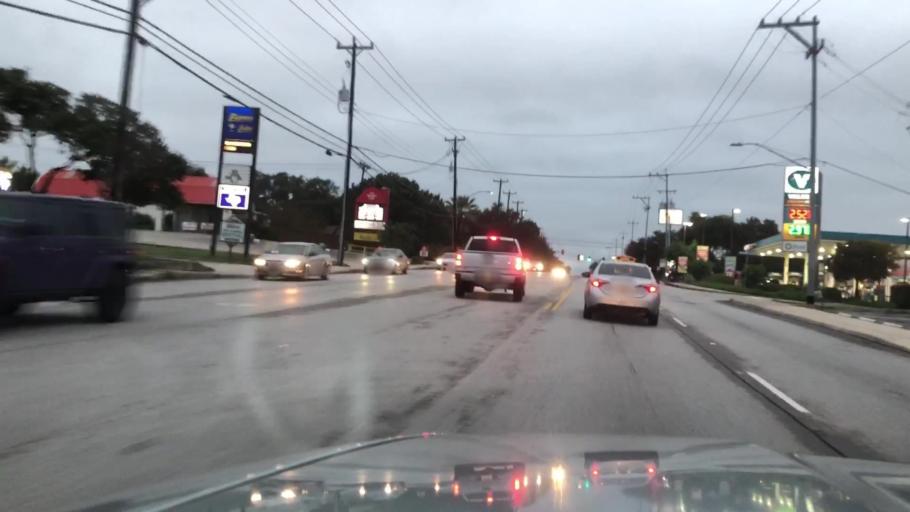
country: US
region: Texas
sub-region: Bexar County
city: Shavano Park
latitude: 29.5631
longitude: -98.6008
